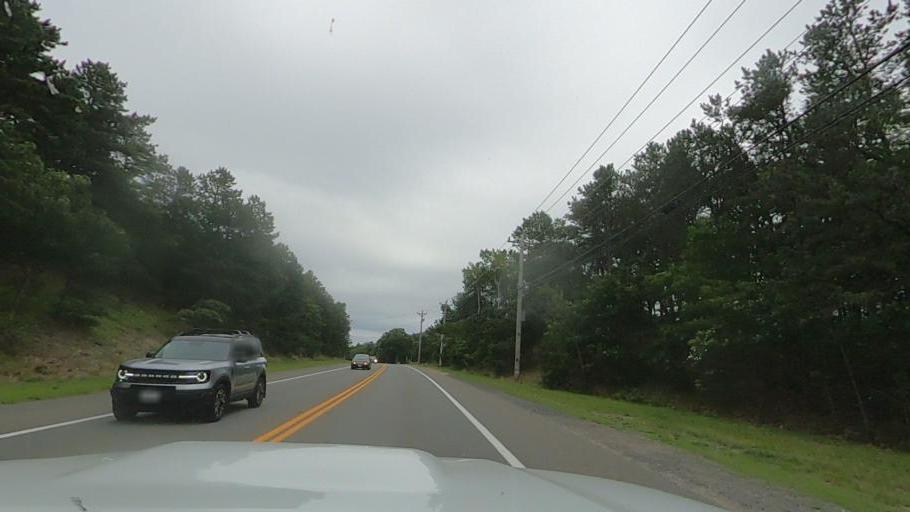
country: US
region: Massachusetts
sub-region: Barnstable County
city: Truro
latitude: 41.9821
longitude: -70.0437
